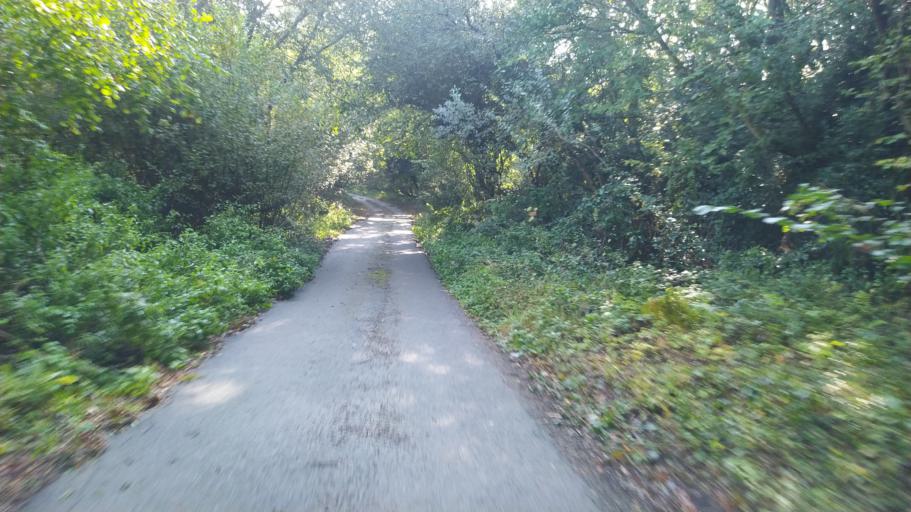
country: GB
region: England
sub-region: Dorset
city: Shaftesbury
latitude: 51.0296
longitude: -2.1449
